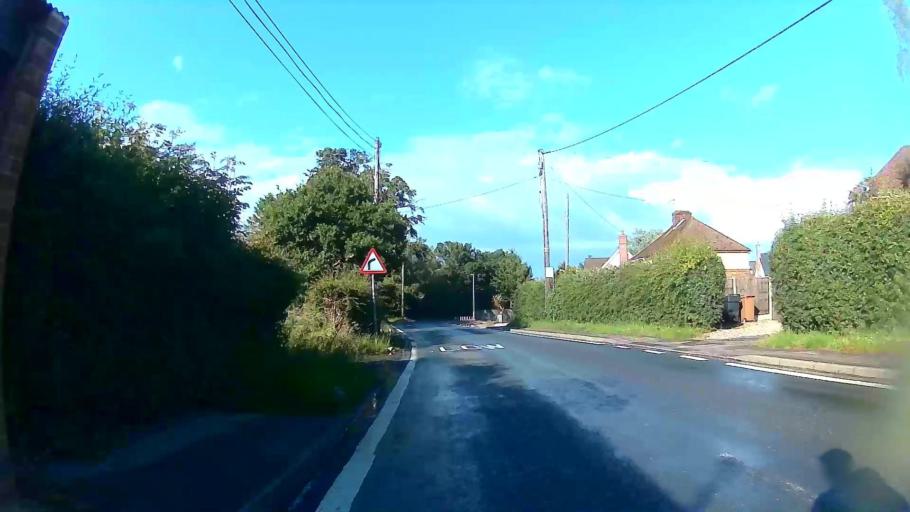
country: GB
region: England
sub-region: Essex
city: Writtle
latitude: 51.7143
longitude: 0.3888
